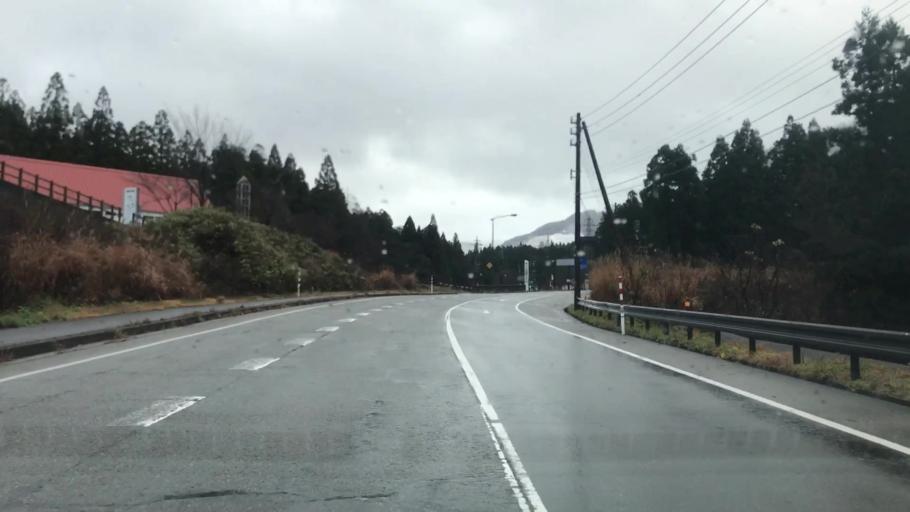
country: JP
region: Toyama
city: Kamiichi
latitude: 36.5774
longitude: 137.4154
